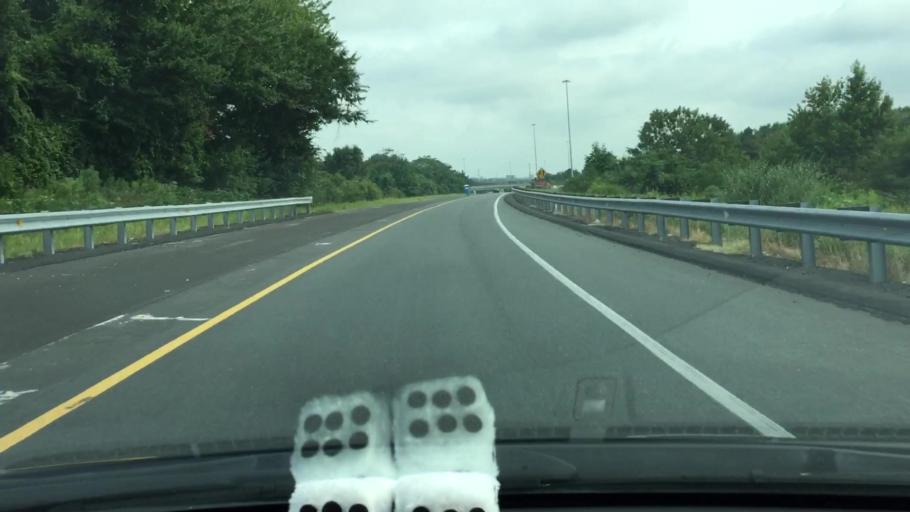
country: US
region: Delaware
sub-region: New Castle County
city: Newport
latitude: 39.7077
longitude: -75.5889
